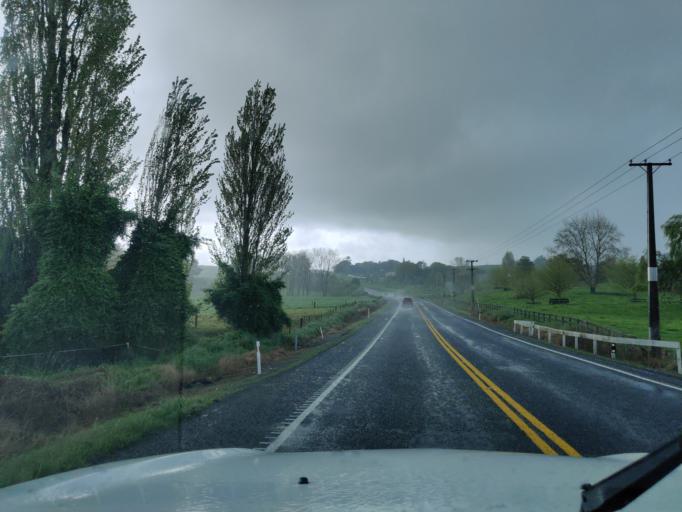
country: NZ
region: Waikato
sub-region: Matamata-Piako District
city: Matamata
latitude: -37.9848
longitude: 175.7104
